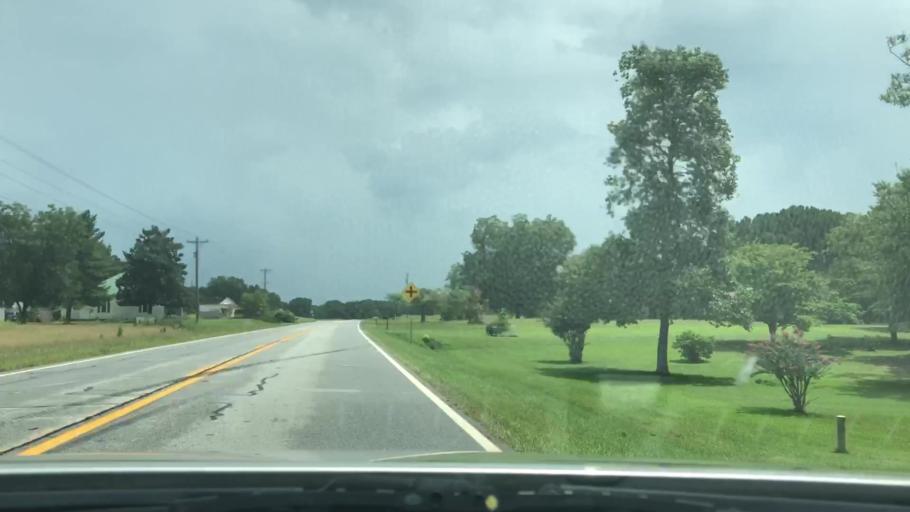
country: US
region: Georgia
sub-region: Pike County
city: Zebulon
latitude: 33.1026
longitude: -84.2986
